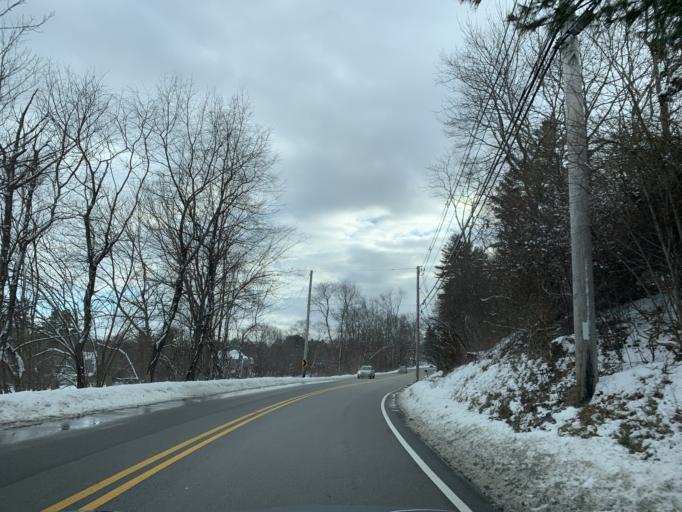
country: US
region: Massachusetts
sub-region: Norfolk County
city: Franklin
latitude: 42.0514
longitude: -71.4354
